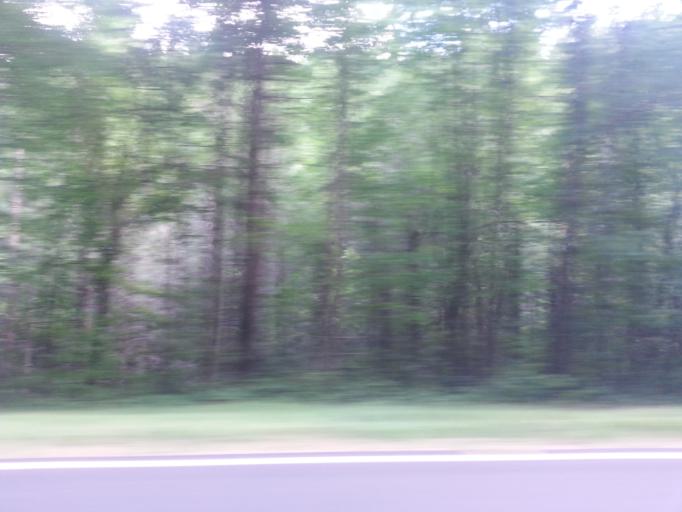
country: US
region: Georgia
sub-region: Towns County
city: Hiawassee
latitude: 34.8330
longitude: -83.7520
